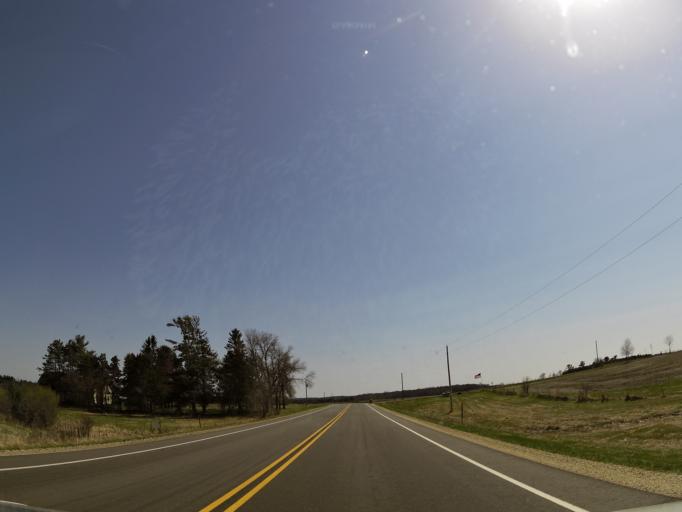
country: US
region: Wisconsin
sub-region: Saint Croix County
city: Hammond
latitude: 44.8746
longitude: -92.4357
